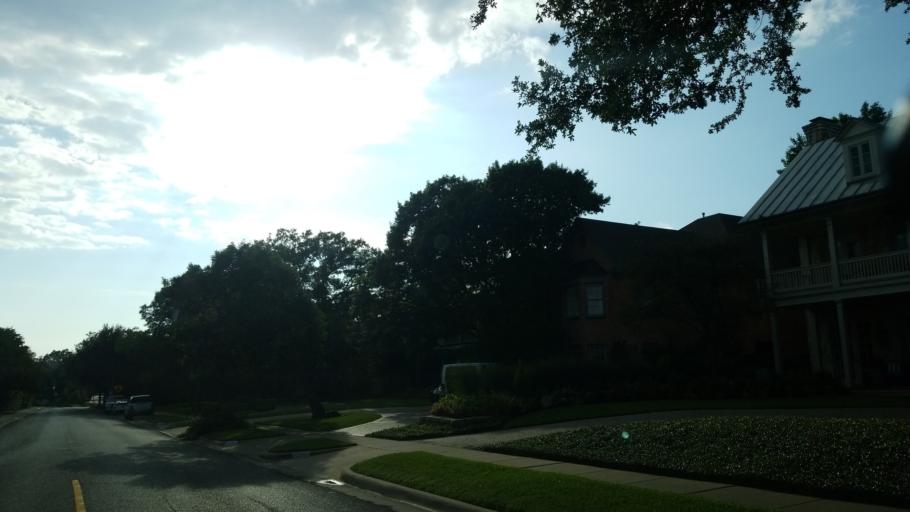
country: US
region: Texas
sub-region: Dallas County
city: University Park
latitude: 32.8439
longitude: -96.7957
